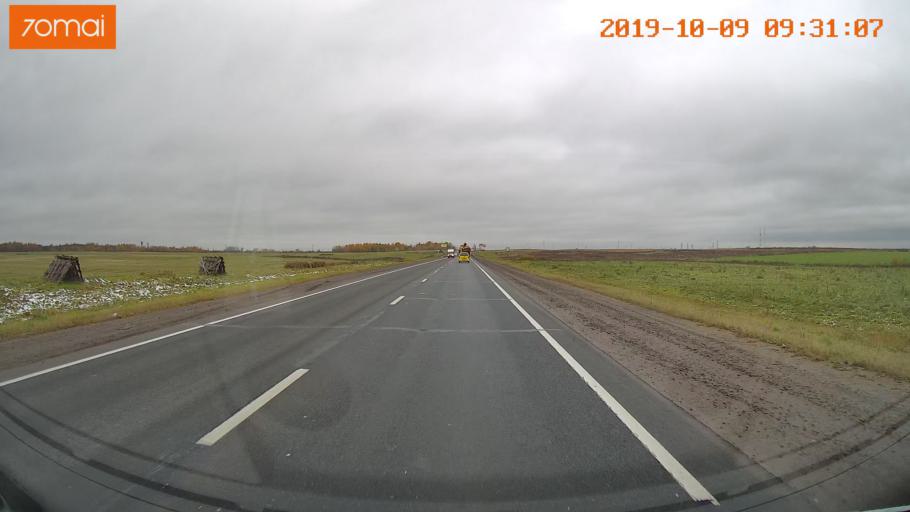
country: RU
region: Vologda
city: Vologda
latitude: 59.1466
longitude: 39.9419
